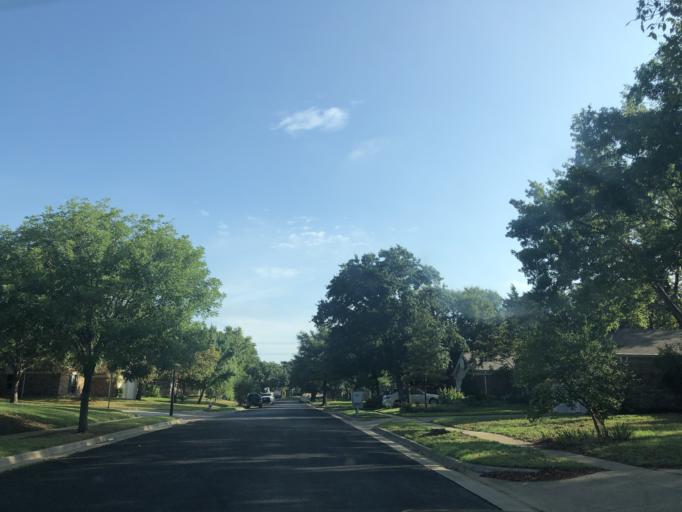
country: US
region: Texas
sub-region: Tarrant County
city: Euless
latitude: 32.8680
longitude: -97.0781
